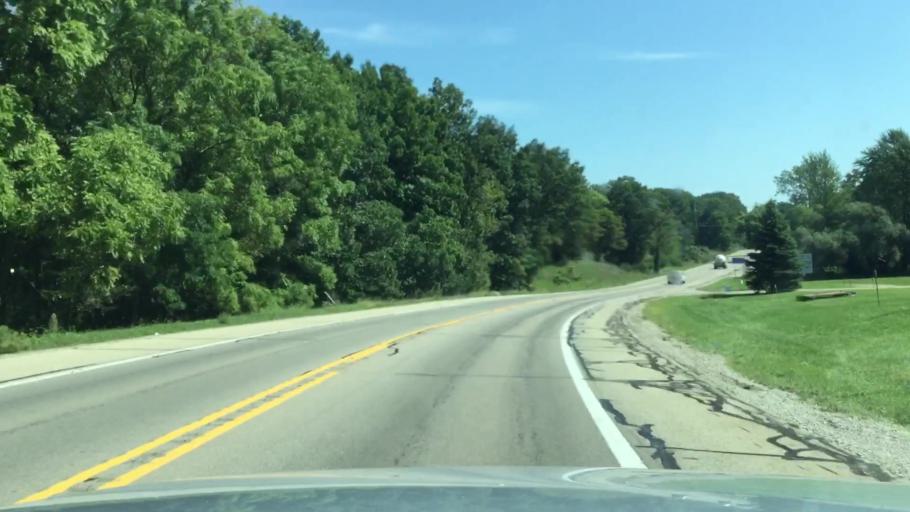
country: US
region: Michigan
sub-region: Jackson County
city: Brooklyn
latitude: 42.0589
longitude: -84.1339
